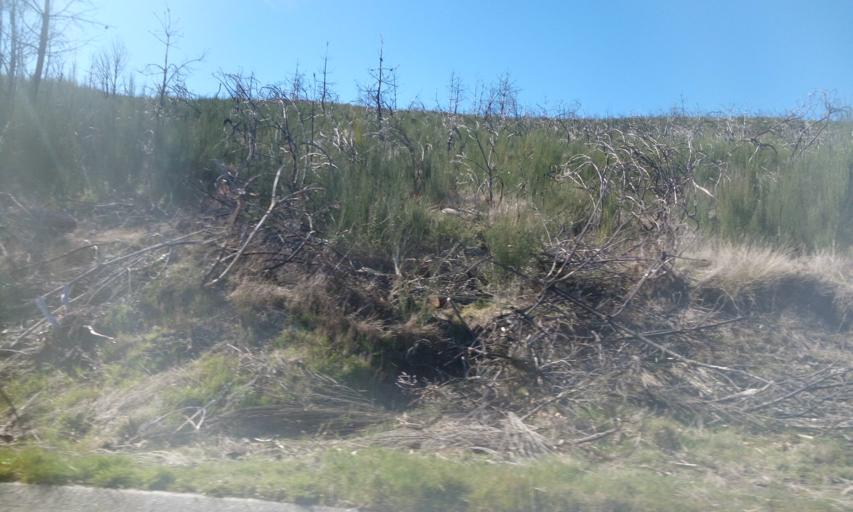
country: PT
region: Guarda
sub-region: Manteigas
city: Manteigas
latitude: 40.4917
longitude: -7.5420
